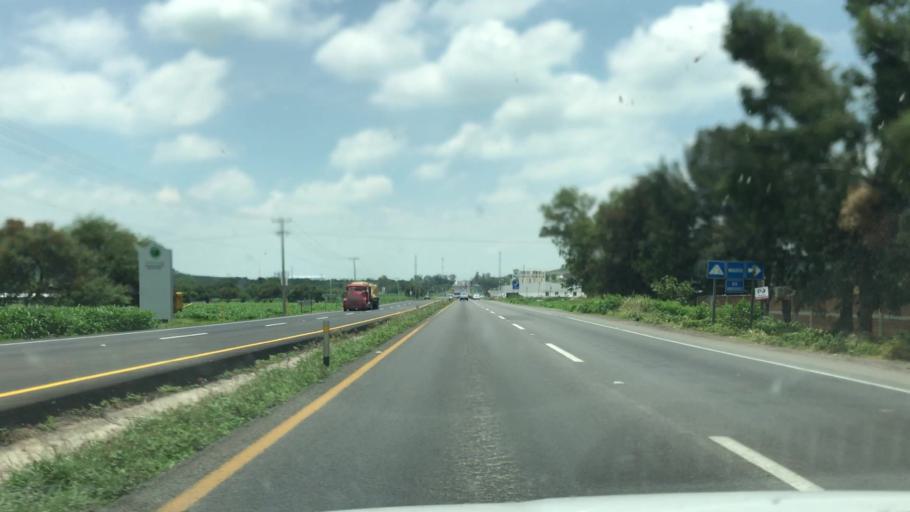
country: MX
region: Guanajuato
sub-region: Irapuato
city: San Ignacio de Rivera (Ojo de Agua)
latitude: 20.5477
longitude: -101.4539
